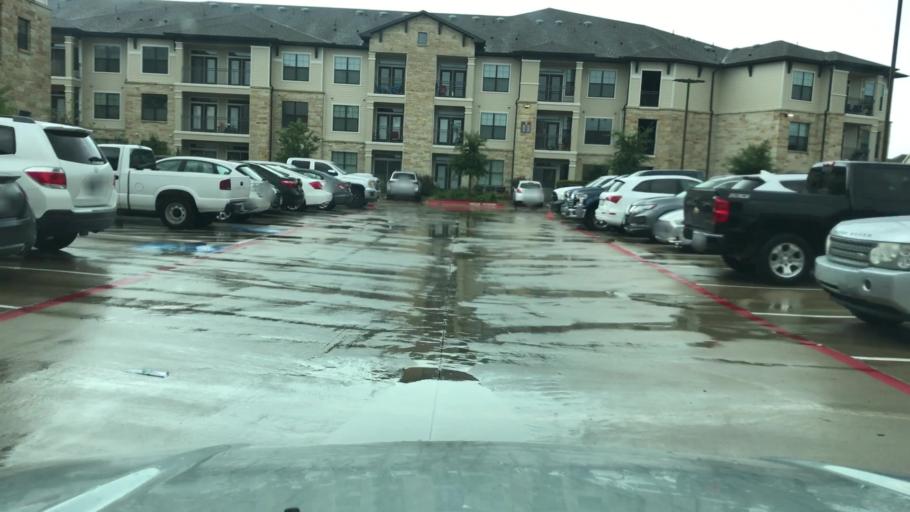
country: US
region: Texas
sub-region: Fort Bend County
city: Cinco Ranch
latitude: 29.7398
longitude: -95.7972
